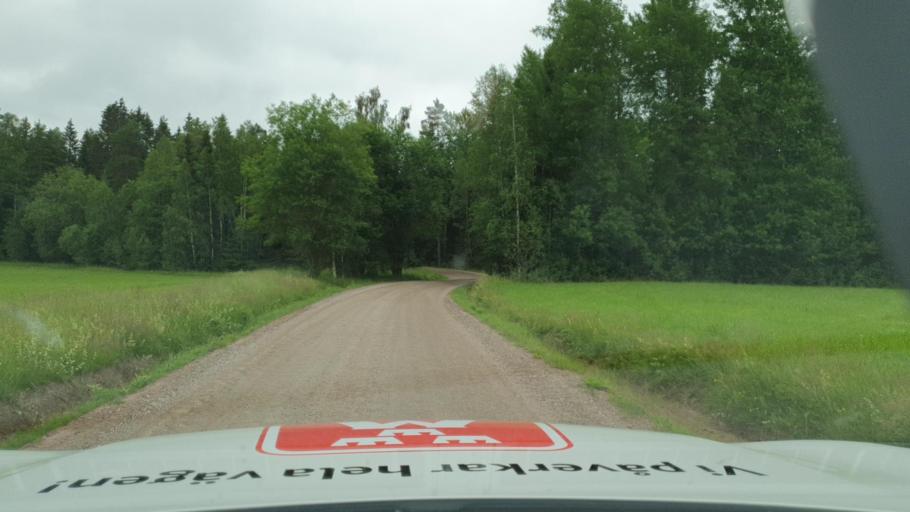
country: SE
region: Vaermland
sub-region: Kristinehamns Kommun
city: Kristinehamn
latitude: 59.5344
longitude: 13.9660
